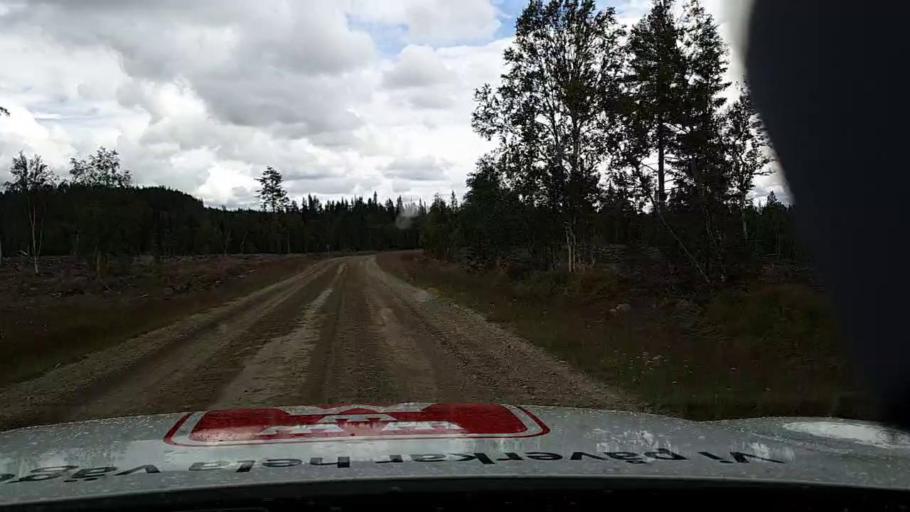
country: SE
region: Jaemtland
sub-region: Are Kommun
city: Jarpen
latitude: 62.6092
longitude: 13.2077
